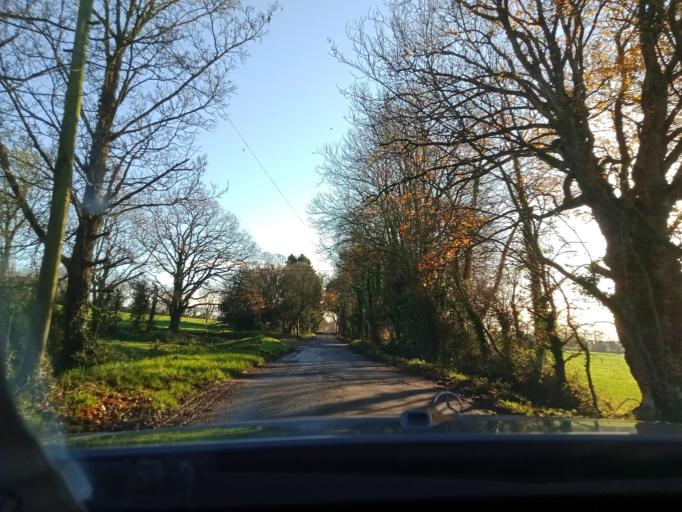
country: IE
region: Leinster
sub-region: Kilkenny
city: Mooncoin
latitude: 52.3454
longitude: -7.2765
